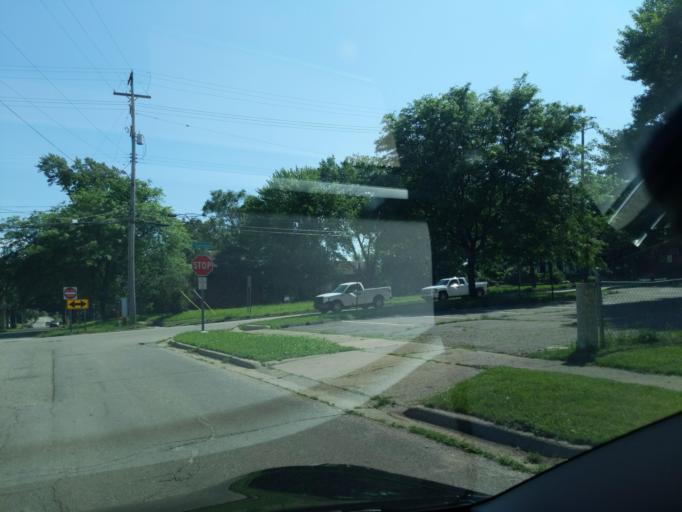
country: US
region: Michigan
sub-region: Jackson County
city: Jackson
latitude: 42.2550
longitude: -84.4119
